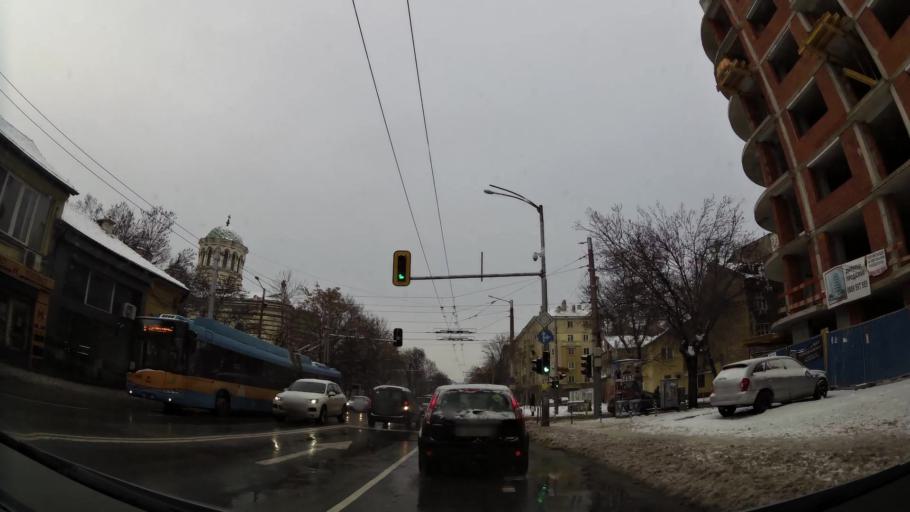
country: BG
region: Sofia-Capital
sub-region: Stolichna Obshtina
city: Sofia
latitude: 42.7009
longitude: 23.3104
